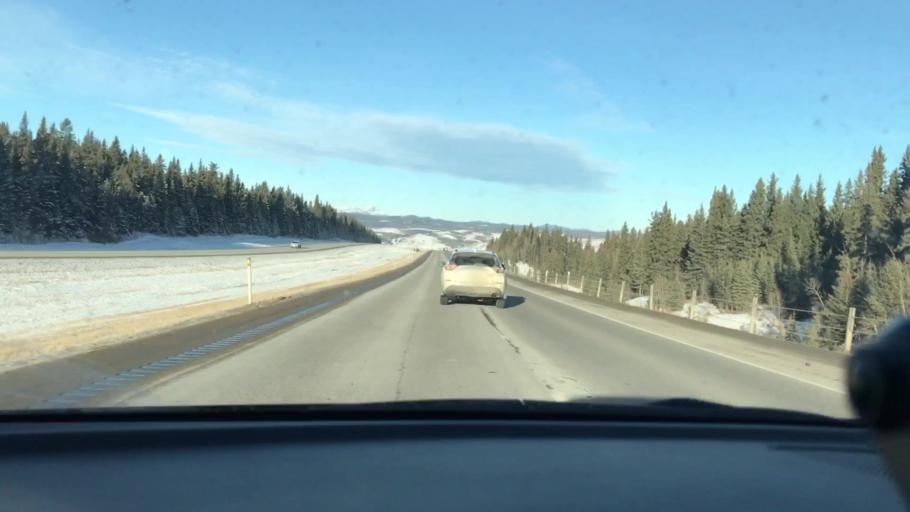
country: CA
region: Alberta
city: Cochrane
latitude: 51.1524
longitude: -114.7425
